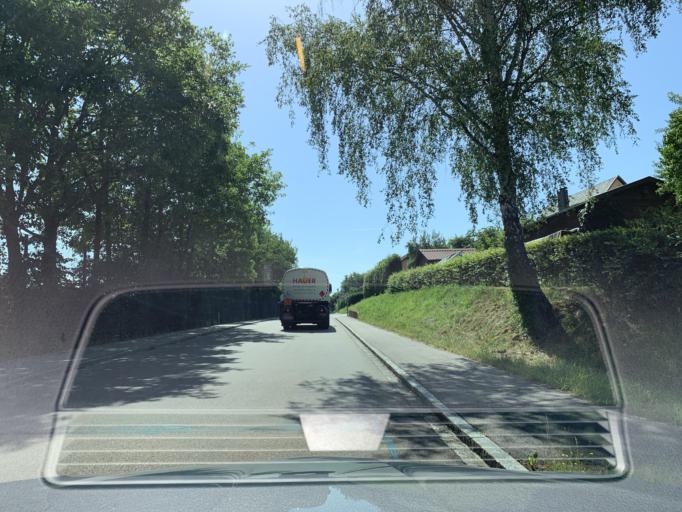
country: DE
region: Bavaria
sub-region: Upper Palatinate
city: Pettendorf
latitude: 49.3488
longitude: 12.3689
